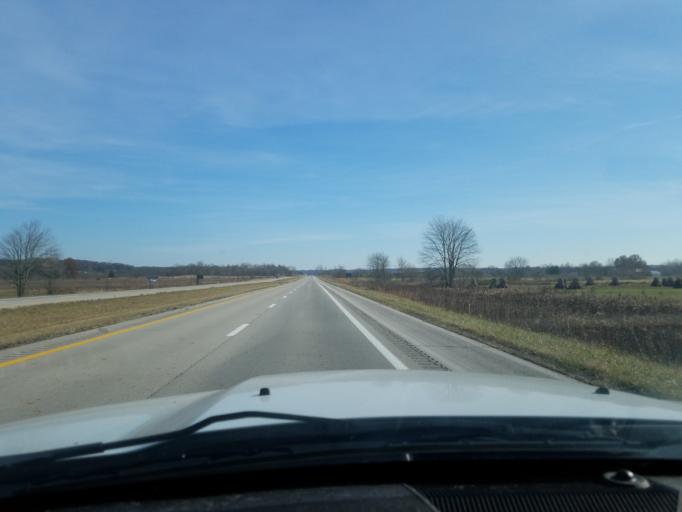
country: US
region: Ohio
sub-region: Jackson County
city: Jackson
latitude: 39.0113
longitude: -82.8025
